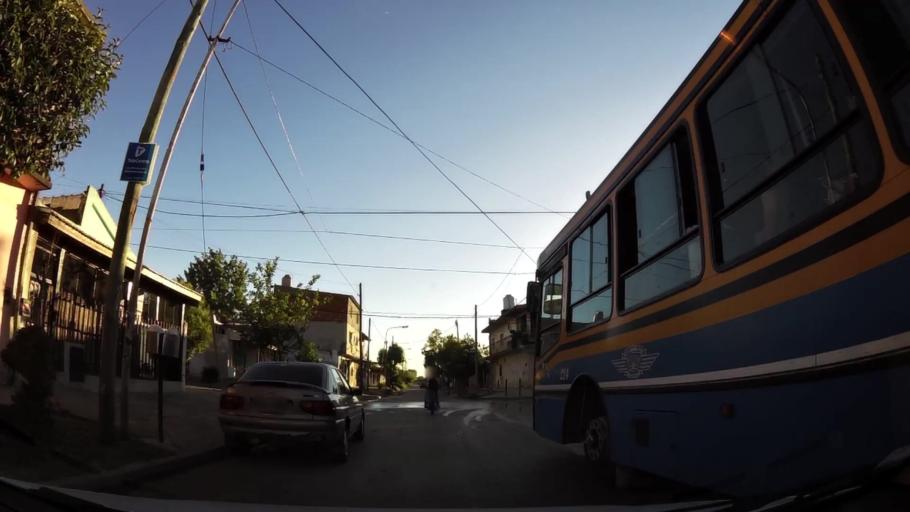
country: AR
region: Buenos Aires
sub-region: Partido de Moron
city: Moron
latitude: -34.7157
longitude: -58.6151
